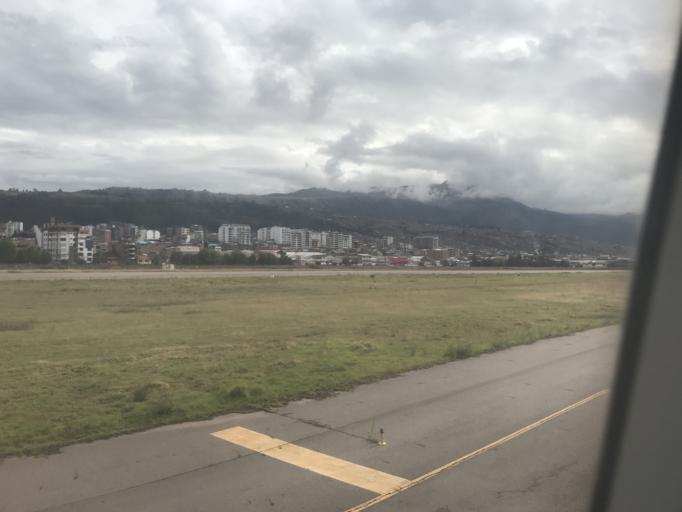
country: PE
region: Cusco
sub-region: Provincia de Cusco
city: Cusco
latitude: -13.5356
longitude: -71.9541
